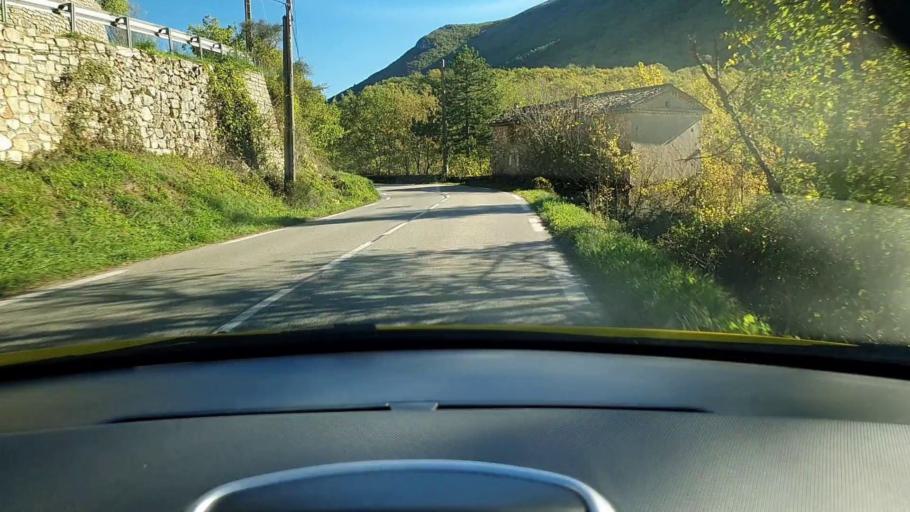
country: FR
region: Languedoc-Roussillon
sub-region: Departement du Gard
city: Aveze
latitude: 43.9704
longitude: 3.5664
